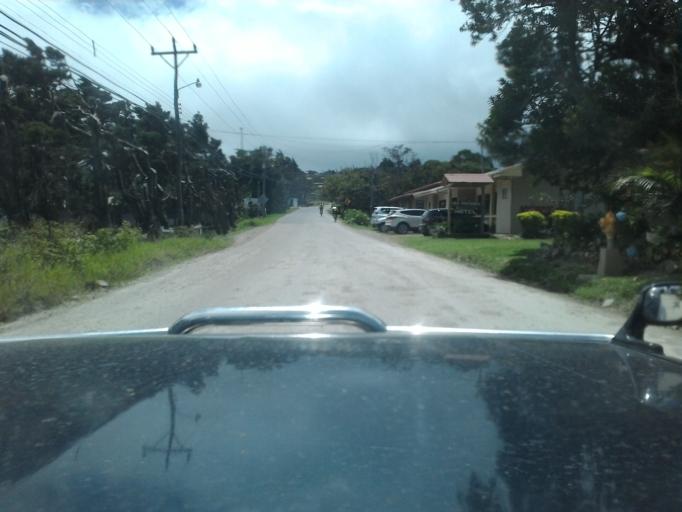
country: CR
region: Guanacaste
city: Juntas
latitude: 10.3127
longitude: -84.8277
